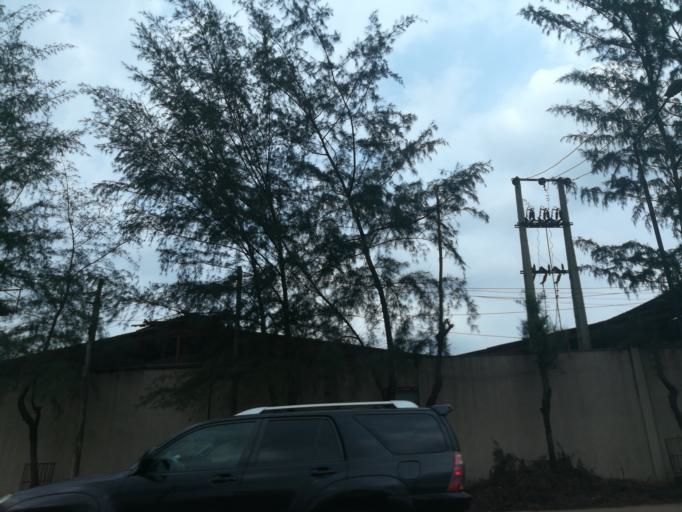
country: NG
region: Lagos
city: Agege
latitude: 6.6230
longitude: 3.3451
